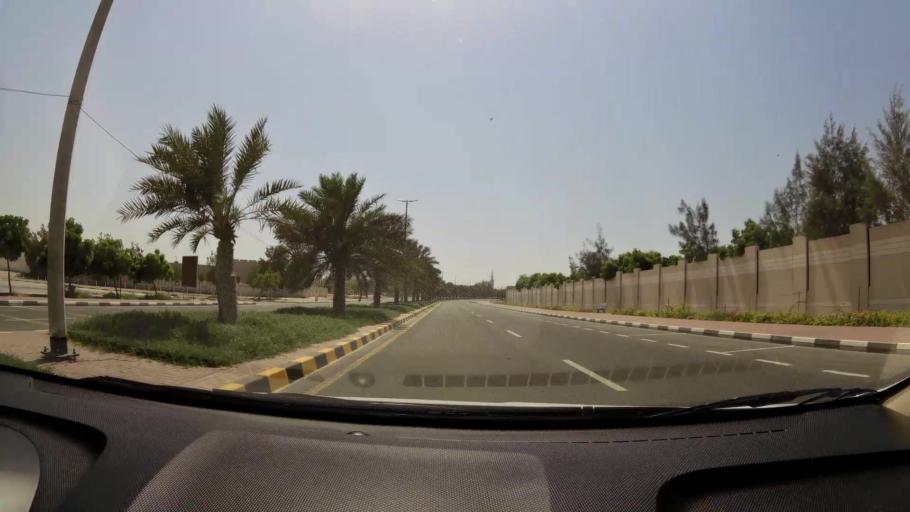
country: AE
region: Ajman
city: Ajman
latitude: 25.4211
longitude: 55.4745
